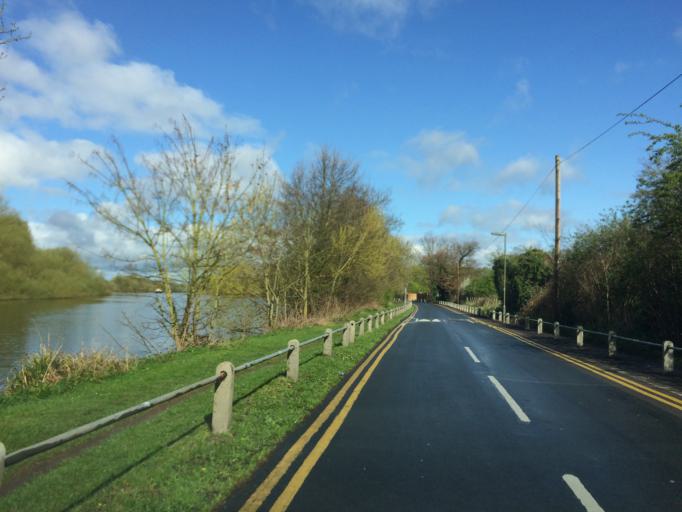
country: GB
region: England
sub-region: Surrey
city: Chertsey
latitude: 51.3958
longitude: -0.4865
